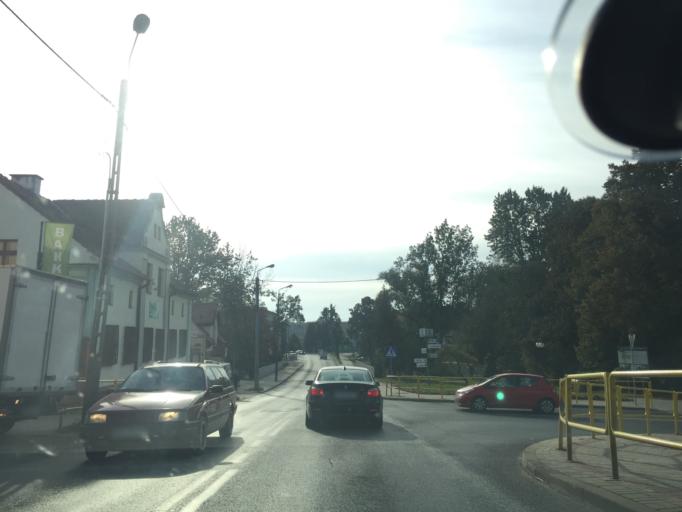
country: PL
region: Warmian-Masurian Voivodeship
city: Dobre Miasto
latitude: 53.9887
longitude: 20.3957
